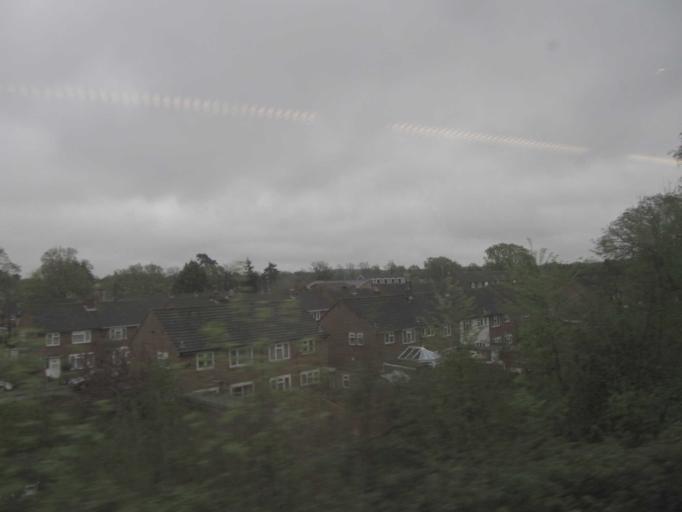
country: GB
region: England
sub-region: Bracknell Forest
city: Sandhurst
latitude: 51.3444
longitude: -0.7999
